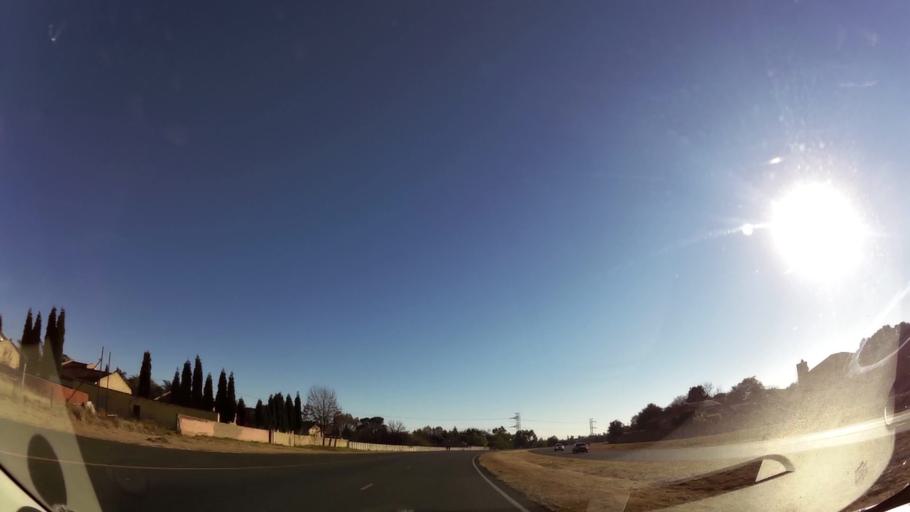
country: ZA
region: Gauteng
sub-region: City of Johannesburg Metropolitan Municipality
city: Modderfontein
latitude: -26.0763
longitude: 28.2030
